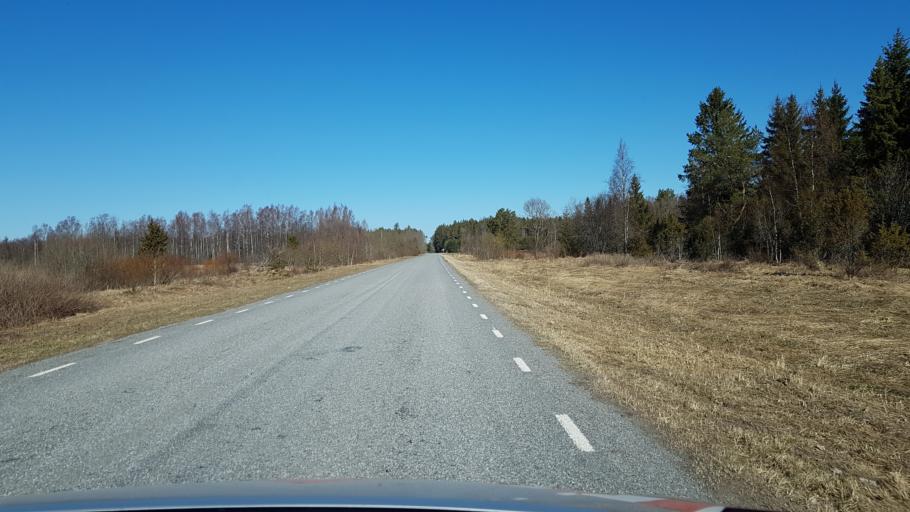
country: EE
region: Laeaene-Virumaa
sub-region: Haljala vald
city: Haljala
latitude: 59.4885
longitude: 26.2470
